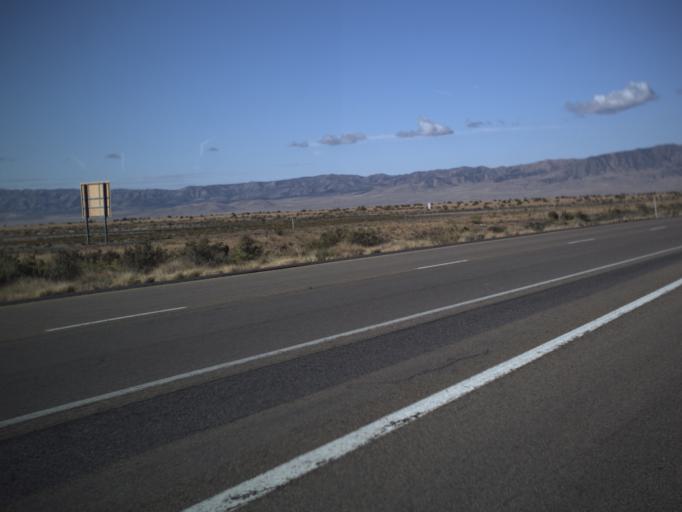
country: US
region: Utah
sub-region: Tooele County
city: Grantsville
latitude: 40.7467
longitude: -112.6583
